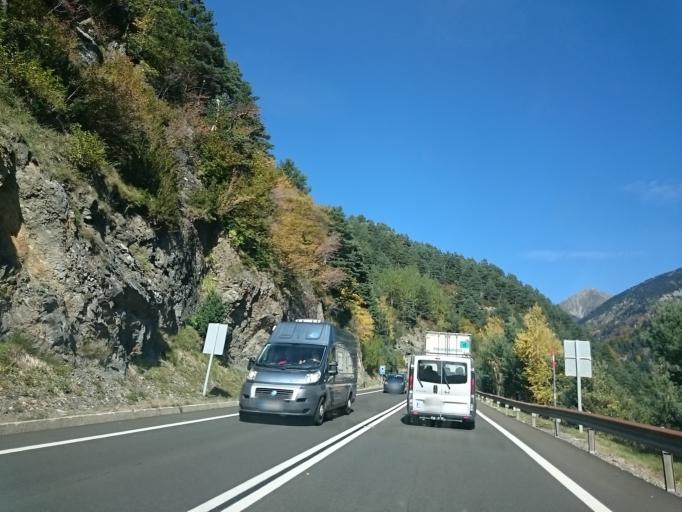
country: ES
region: Catalonia
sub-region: Provincia de Lleida
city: Vielha
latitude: 42.5697
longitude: 0.7546
